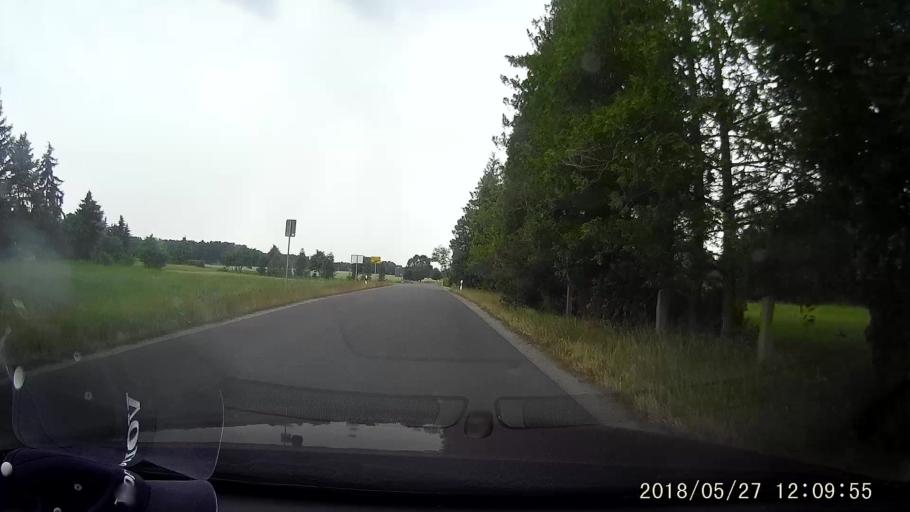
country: DE
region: Saxony
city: Klitten
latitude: 51.3519
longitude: 14.5933
